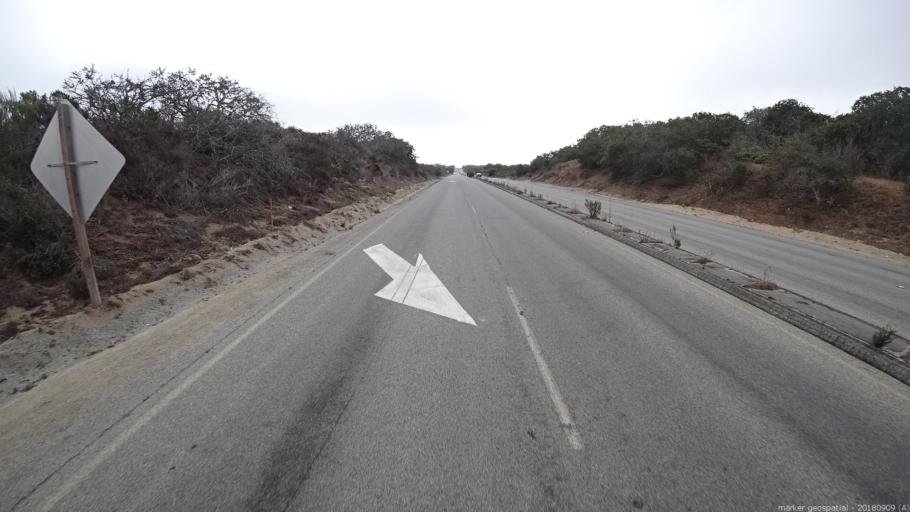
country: US
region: California
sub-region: Monterey County
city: Marina
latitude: 36.6651
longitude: -121.7528
